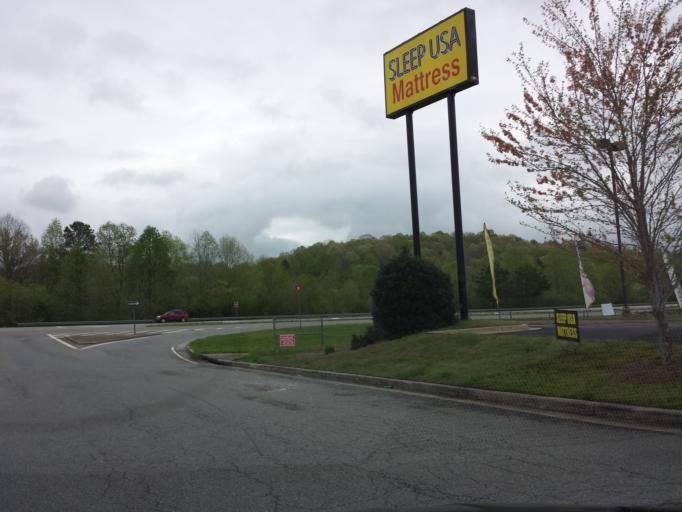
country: US
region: Georgia
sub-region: Pickens County
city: Nelson
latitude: 34.3970
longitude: -84.4136
